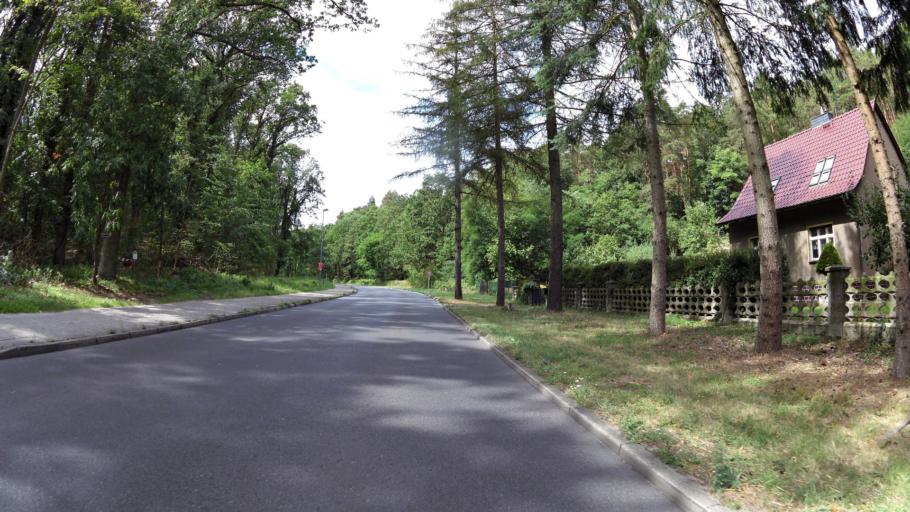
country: DE
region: Brandenburg
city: Neuzelle
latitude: 52.0951
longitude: 14.6459
